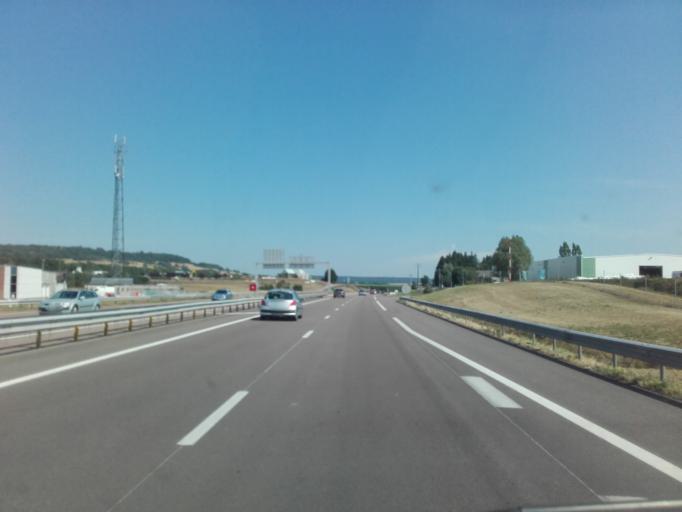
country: FR
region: Bourgogne
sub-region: Departement de la Cote-d'Or
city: Pouilly-en-Auxois
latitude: 47.2512
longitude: 4.5596
